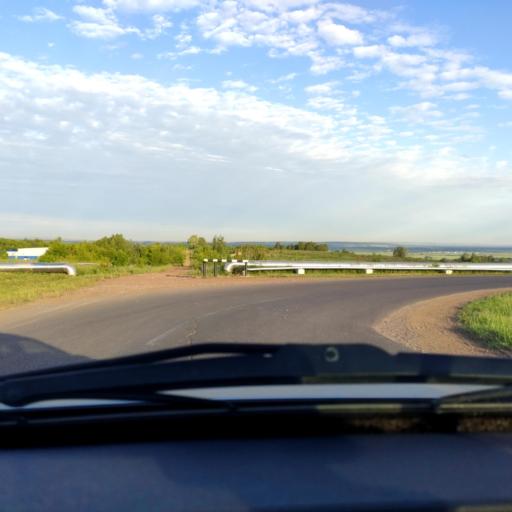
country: RU
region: Bashkortostan
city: Blagoveshchensk
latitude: 54.9095
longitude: 56.0545
